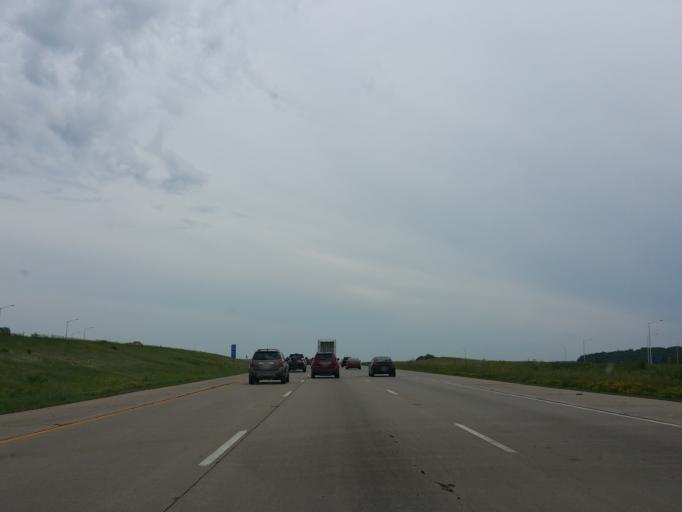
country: US
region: Wisconsin
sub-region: Columbia County
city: Poynette
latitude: 43.4298
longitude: -89.4820
